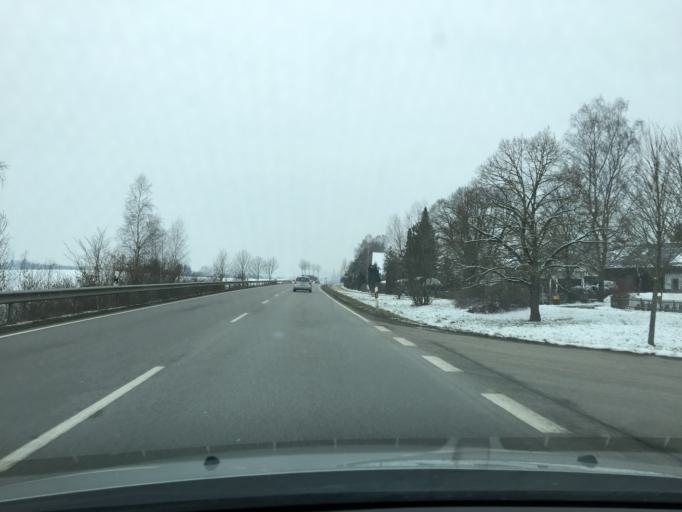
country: DE
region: Bavaria
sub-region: Lower Bavaria
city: Geisenhausen
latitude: 48.4701
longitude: 12.2879
